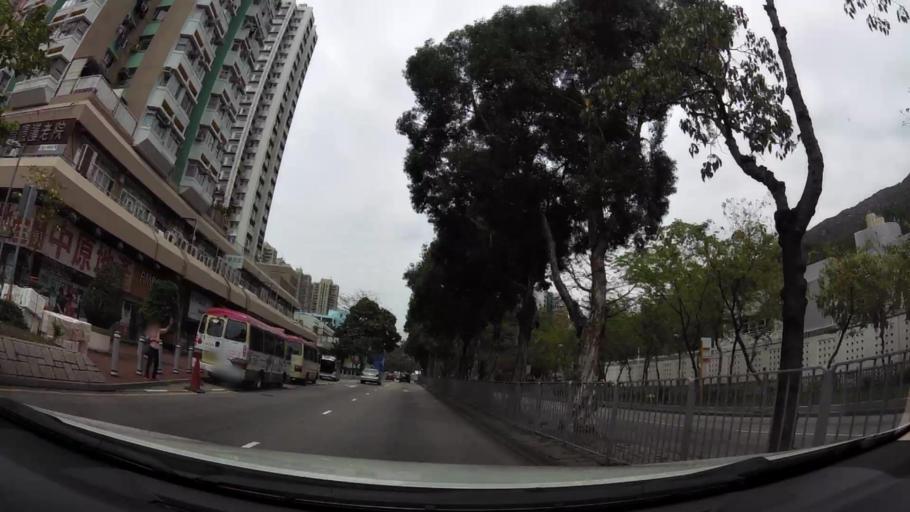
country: HK
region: Tuen Mun
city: Tuen Mun
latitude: 22.3888
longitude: 113.9803
